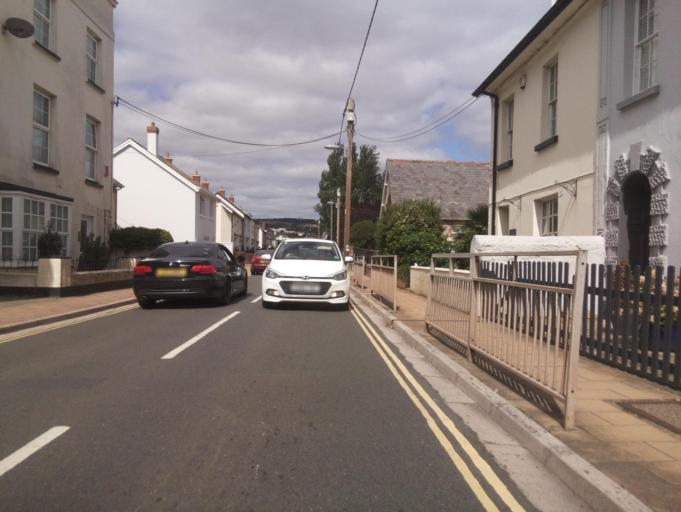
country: GB
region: England
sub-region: Devon
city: Teignmouth
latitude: 50.5404
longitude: -3.5094
